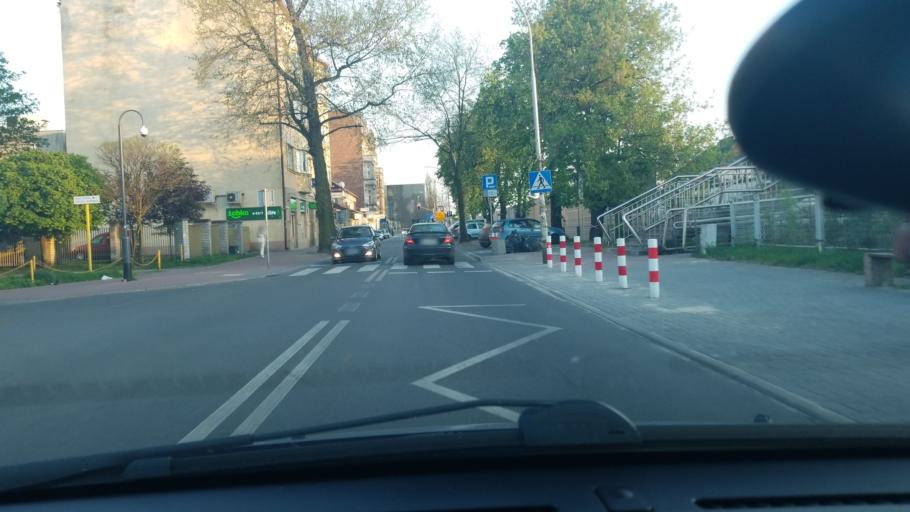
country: PL
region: Silesian Voivodeship
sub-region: Czestochowa
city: Czestochowa
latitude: 50.8135
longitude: 19.1218
